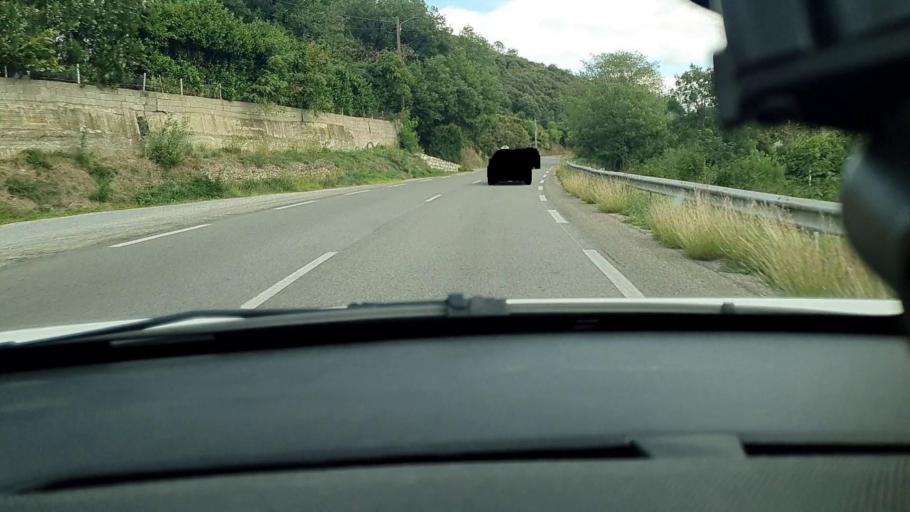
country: FR
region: Languedoc-Roussillon
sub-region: Departement du Gard
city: Les Mages
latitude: 44.2293
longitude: 4.1531
